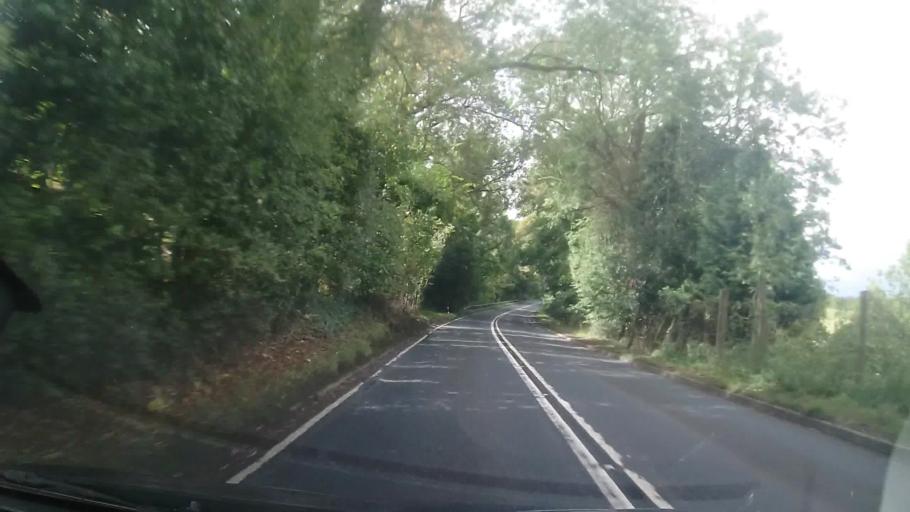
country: GB
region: England
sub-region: Shropshire
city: Romsley
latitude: 52.4263
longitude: -2.3018
